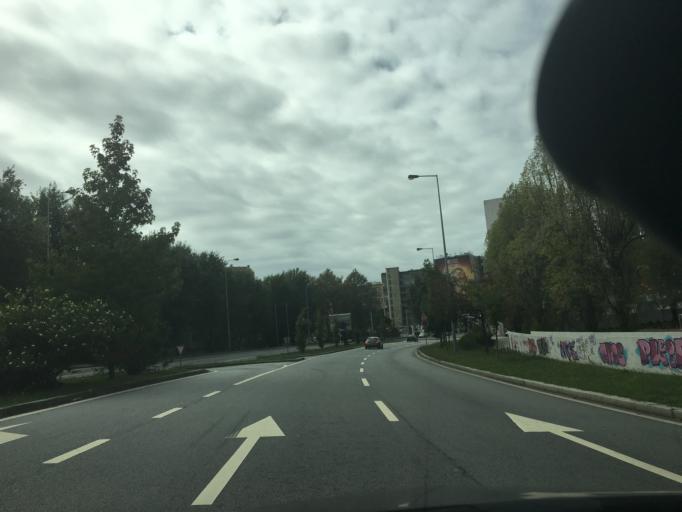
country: PT
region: Porto
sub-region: Matosinhos
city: Matosinhos
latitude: 41.1813
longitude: -8.6786
